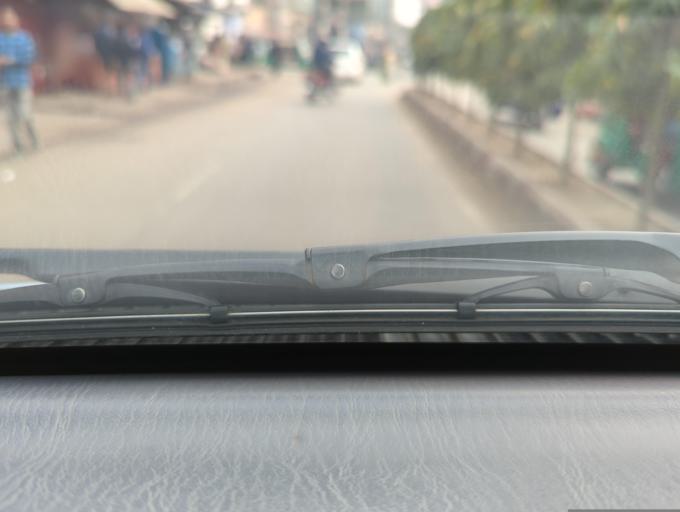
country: BD
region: Sylhet
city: Maulavi Bazar
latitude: 24.4882
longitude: 91.7636
